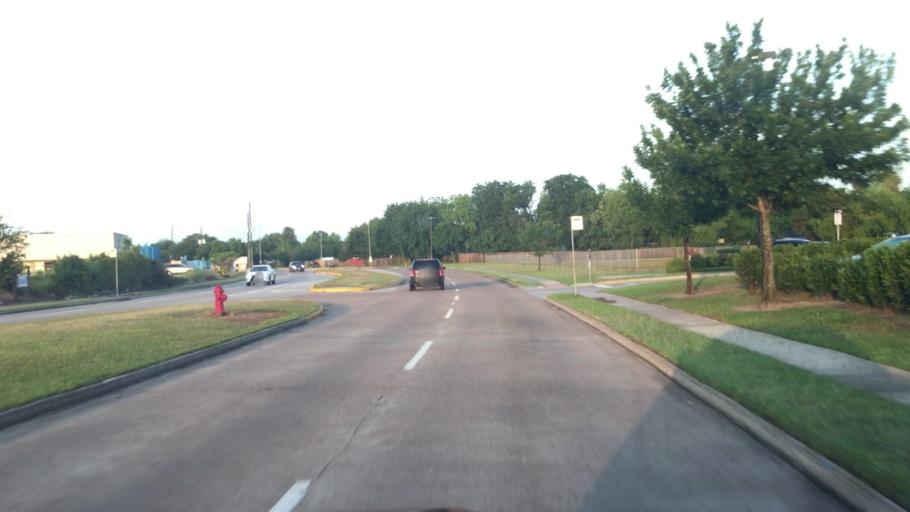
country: US
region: Texas
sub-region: Harris County
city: Hudson
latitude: 29.9600
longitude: -95.4801
